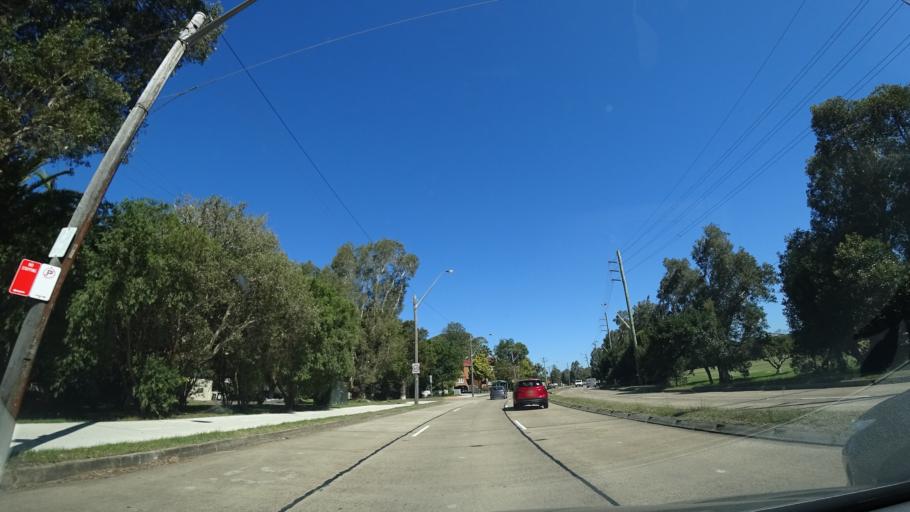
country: AU
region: New South Wales
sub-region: Warringah
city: North Manly
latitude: -33.7770
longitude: 151.2737
